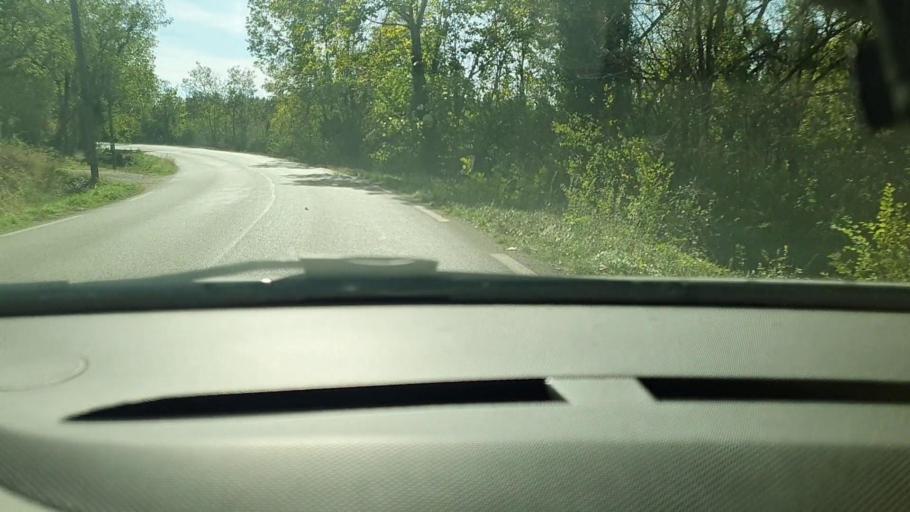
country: FR
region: Languedoc-Roussillon
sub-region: Departement du Gard
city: Saint-Ambroix
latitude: 44.2496
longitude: 4.2129
